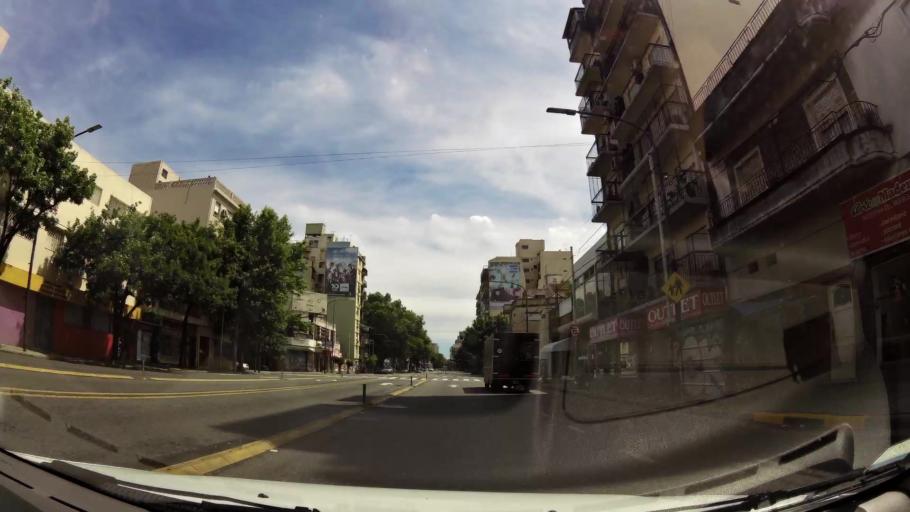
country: AR
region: Buenos Aires F.D.
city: Villa Santa Rita
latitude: -34.6122
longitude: -58.4697
